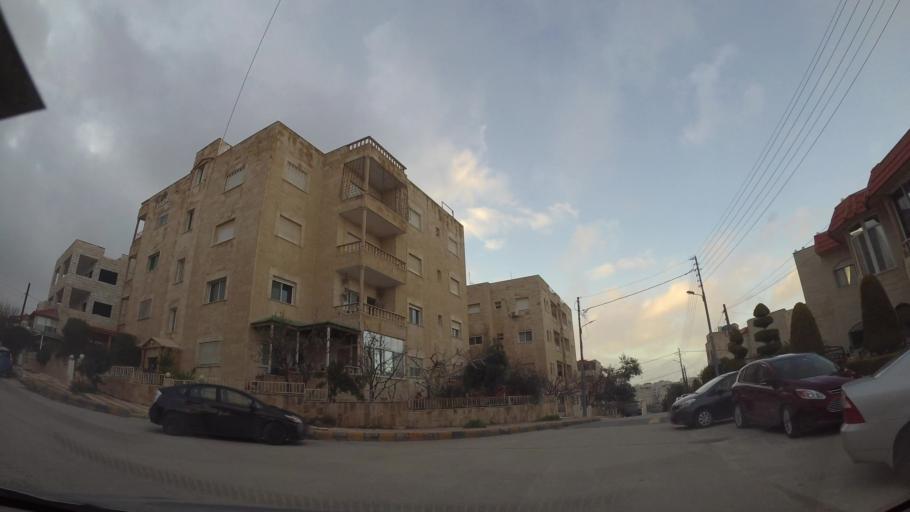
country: JO
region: Amman
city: Al Jubayhah
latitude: 32.0489
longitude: 35.8964
